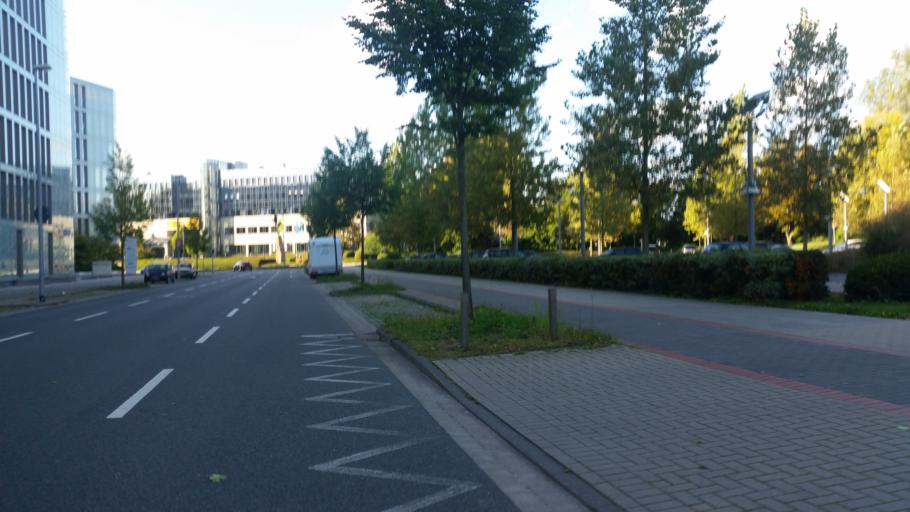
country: DE
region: Lower Saxony
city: Hannover
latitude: 52.4010
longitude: 9.7674
